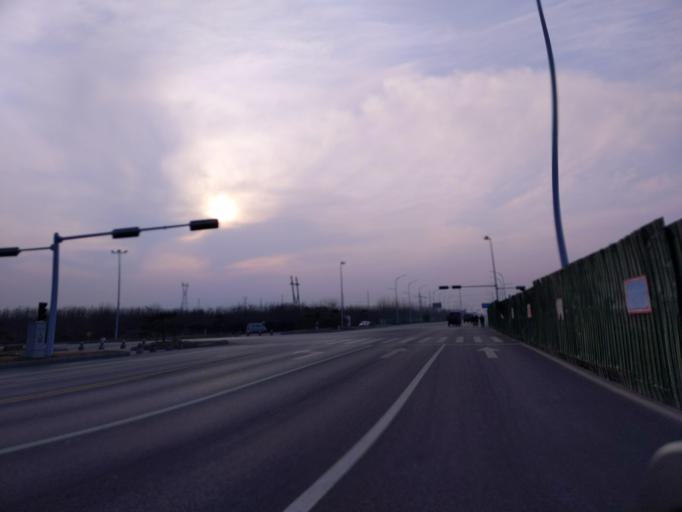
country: CN
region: Henan Sheng
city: Puyang
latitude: 35.8180
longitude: 115.0079
